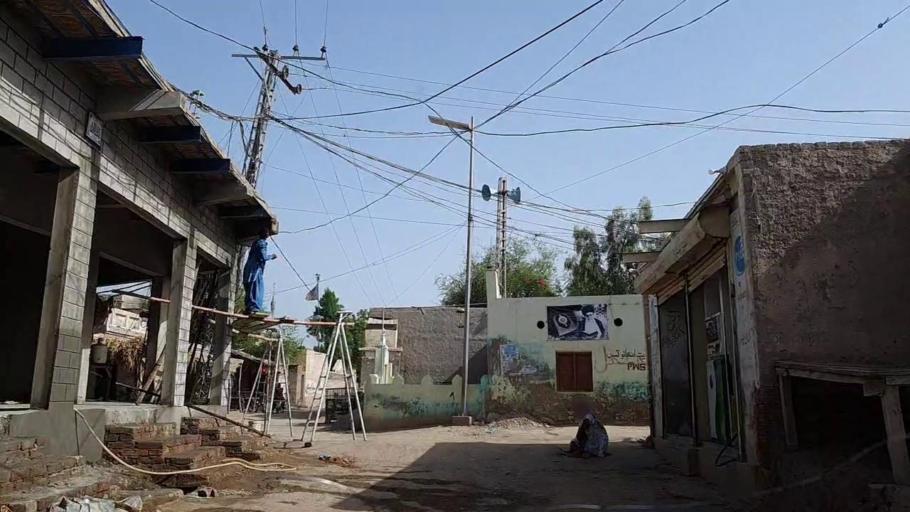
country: PK
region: Sindh
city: Kandiaro
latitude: 27.0636
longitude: 68.2068
